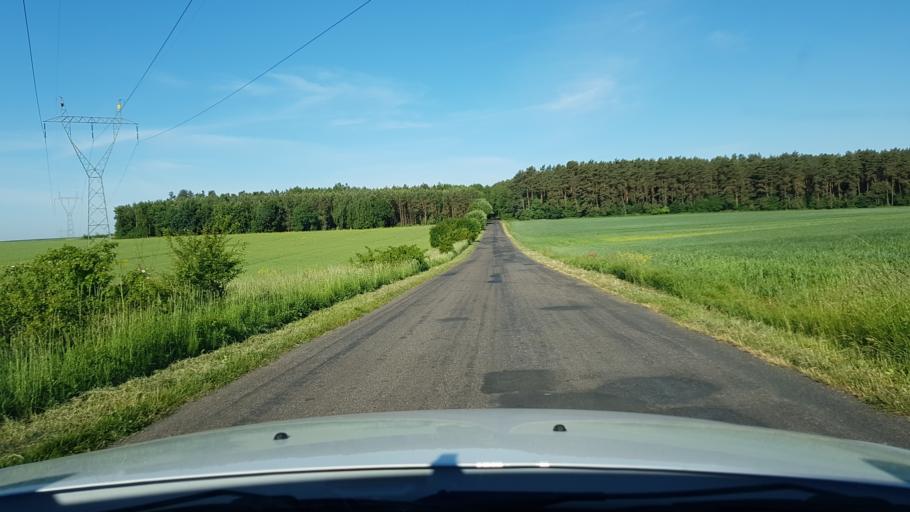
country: PL
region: West Pomeranian Voivodeship
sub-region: Powiat pyrzycki
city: Bielice
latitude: 53.2236
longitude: 14.6300
